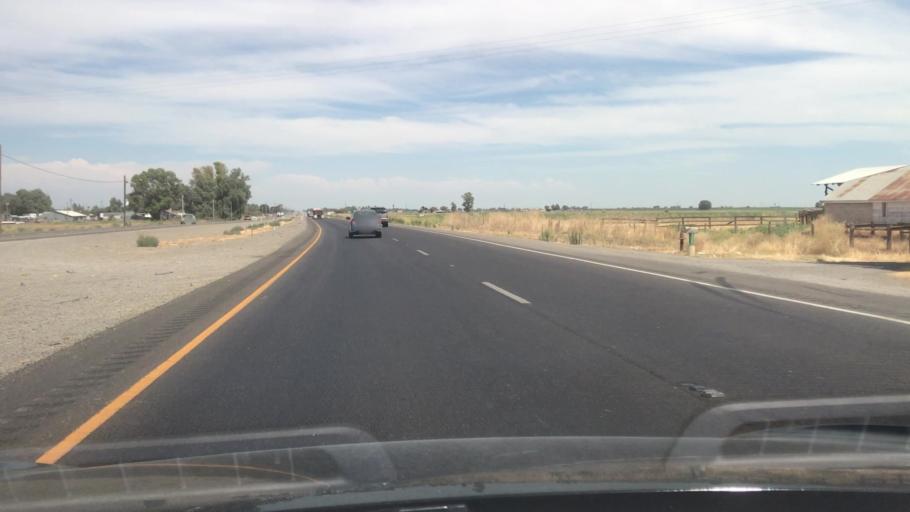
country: US
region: California
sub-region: Merced County
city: Los Banos
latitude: 37.0565
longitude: -120.9366
